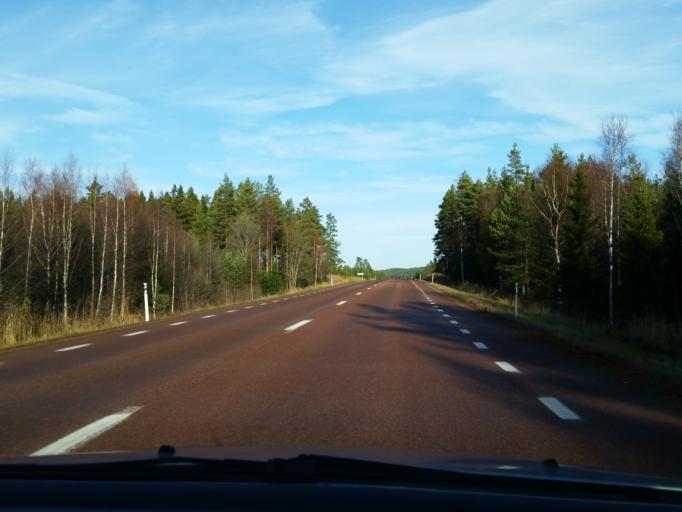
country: AX
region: Alands landsbygd
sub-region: Finstroem
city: Finstroem
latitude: 60.2848
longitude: 19.9527
